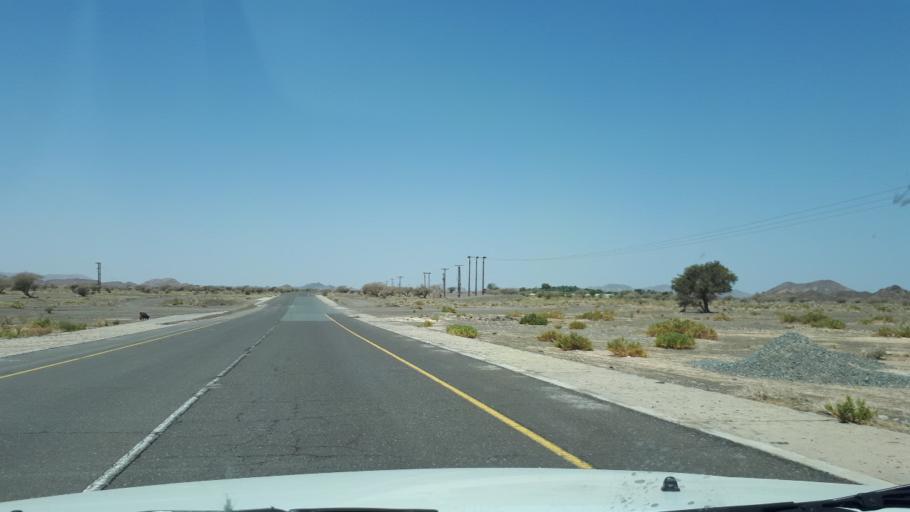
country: OM
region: Ash Sharqiyah
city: Ibra'
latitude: 22.6173
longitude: 58.4292
